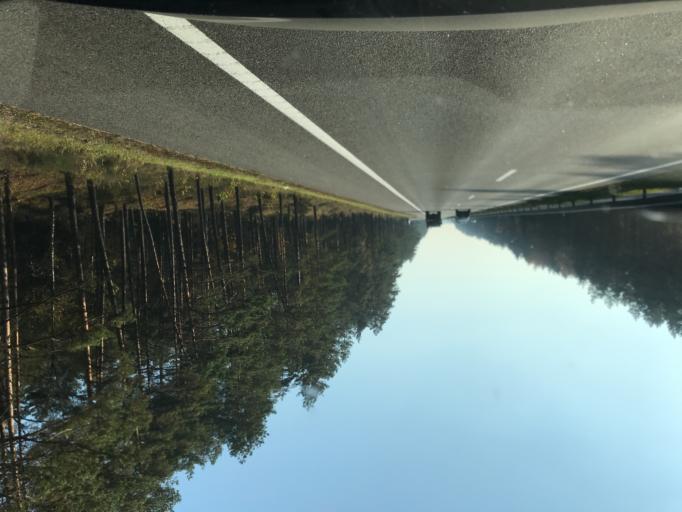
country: BY
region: Minsk
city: Enyerhyetykaw
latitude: 53.5470
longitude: 26.9400
